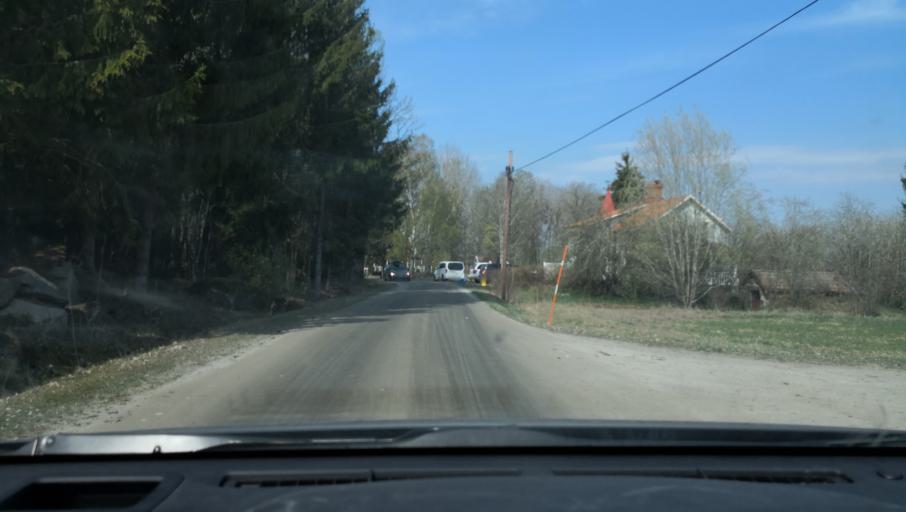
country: SE
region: Vaestmanland
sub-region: Vasteras
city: Skultuna
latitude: 59.7678
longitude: 16.4526
